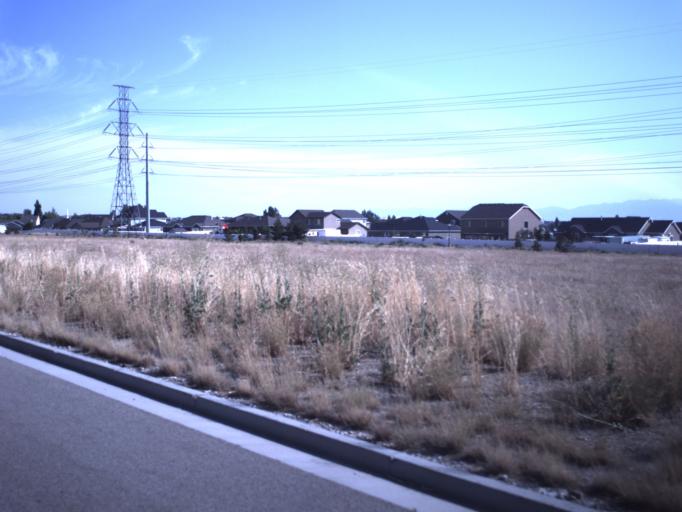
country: US
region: Utah
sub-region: Salt Lake County
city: Herriman
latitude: 40.5293
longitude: -112.0074
